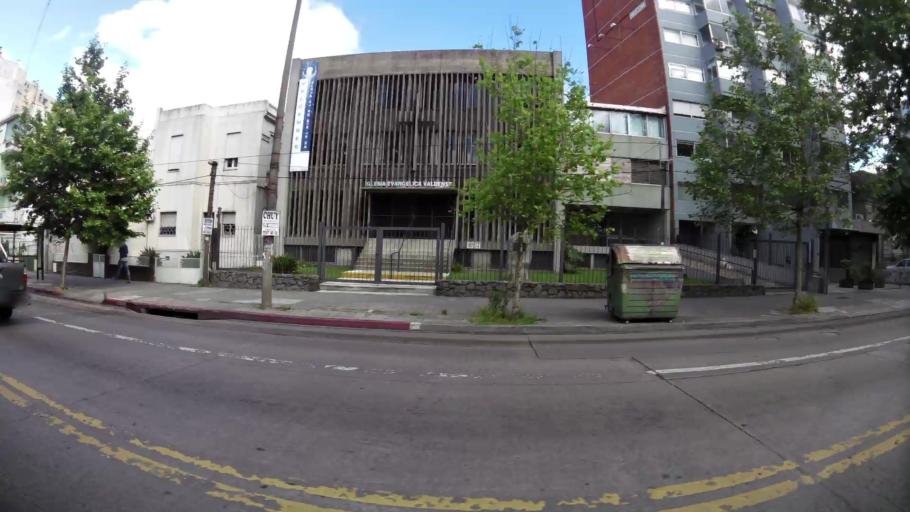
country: UY
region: Montevideo
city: Montevideo
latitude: -34.8833
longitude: -56.1547
